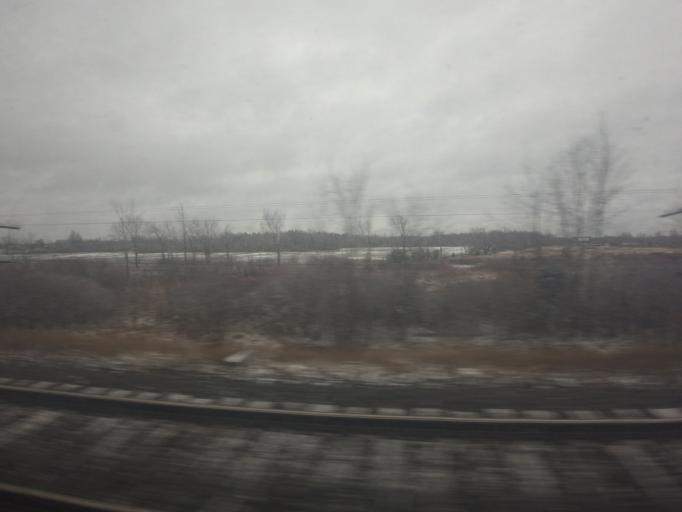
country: US
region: New York
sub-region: Jefferson County
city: Alexandria Bay
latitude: 44.3977
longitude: -76.0276
